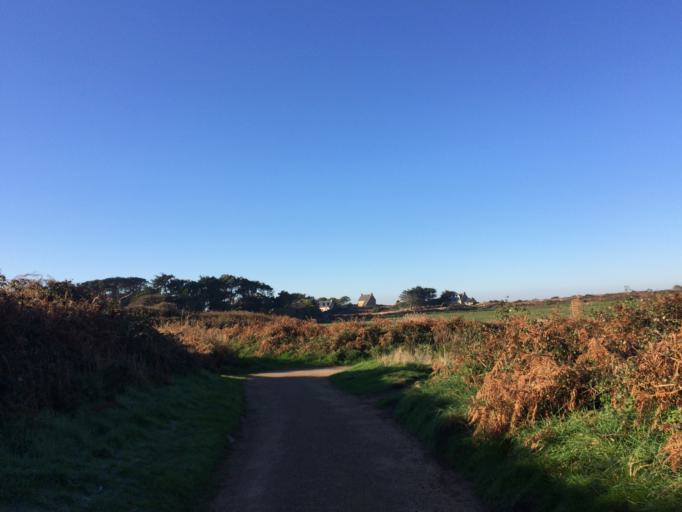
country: FR
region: Brittany
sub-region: Departement des Cotes-d'Armor
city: Ploubazlanec
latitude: 48.8616
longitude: -2.9909
